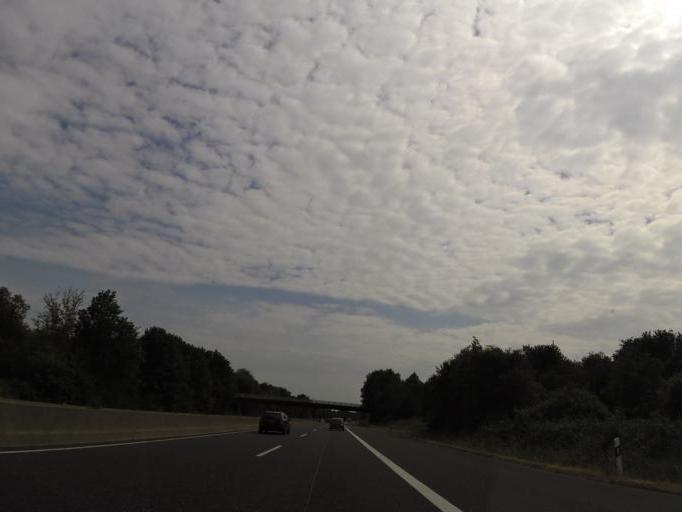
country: DE
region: Hesse
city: Dreieich
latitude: 50.0230
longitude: 8.7097
